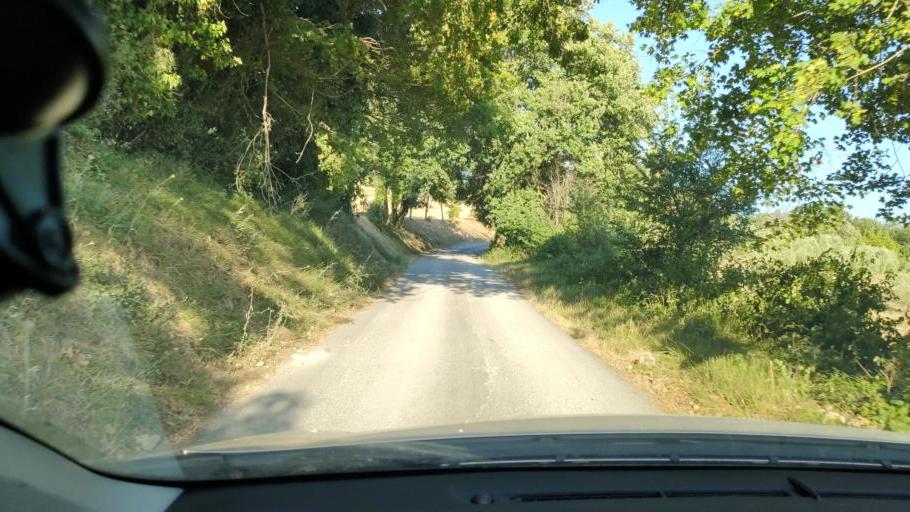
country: IT
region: Umbria
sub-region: Provincia di Terni
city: Amelia
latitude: 42.5446
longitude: 12.3949
